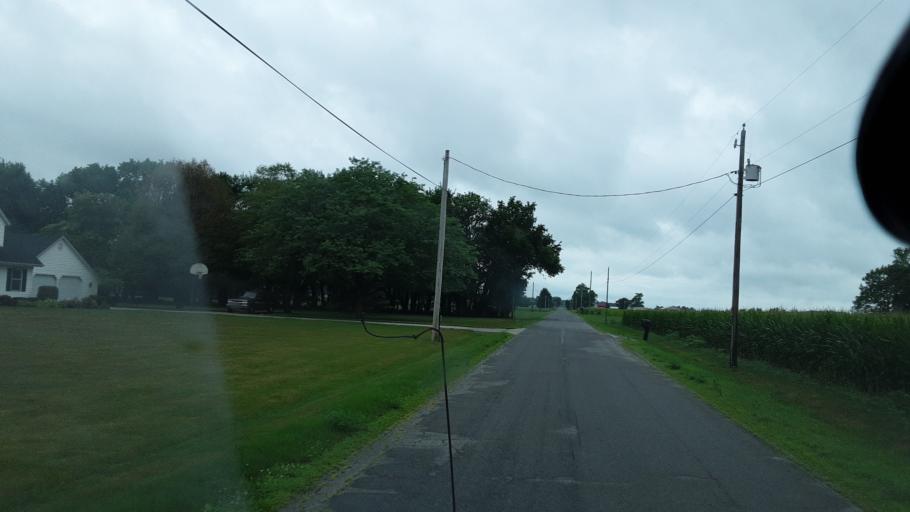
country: US
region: Ohio
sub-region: Van Wert County
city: Convoy
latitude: 40.8224
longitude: -84.7176
